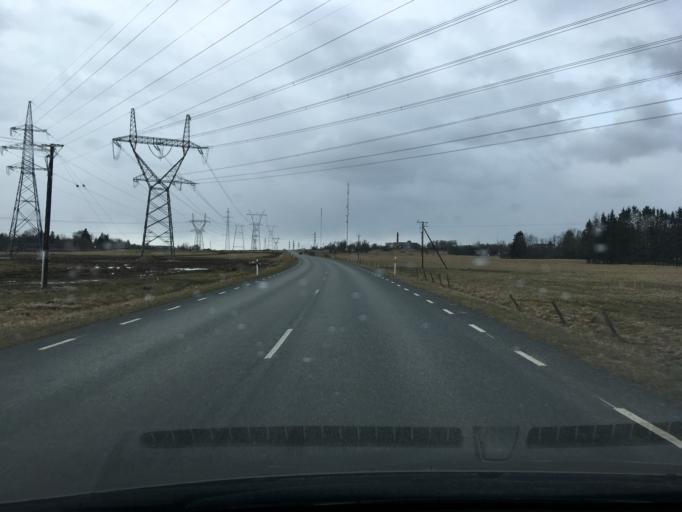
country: EE
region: Laeaene
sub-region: Lihula vald
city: Lihula
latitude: 58.6682
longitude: 23.8316
